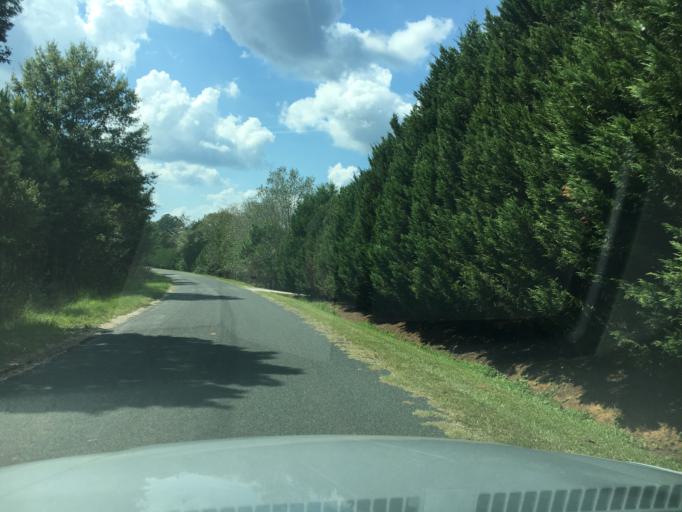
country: US
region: South Carolina
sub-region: Greenwood County
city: Greenwood
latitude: 34.0623
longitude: -82.1506
